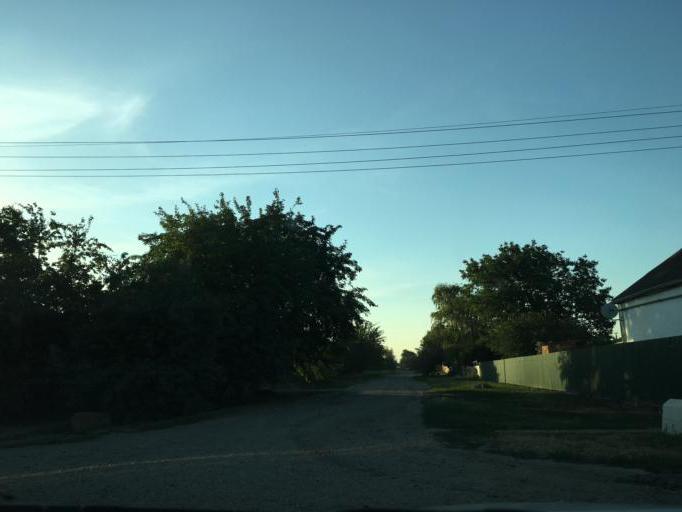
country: RU
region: Krasnodarskiy
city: Kushchevskaya
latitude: 46.5657
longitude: 39.6497
